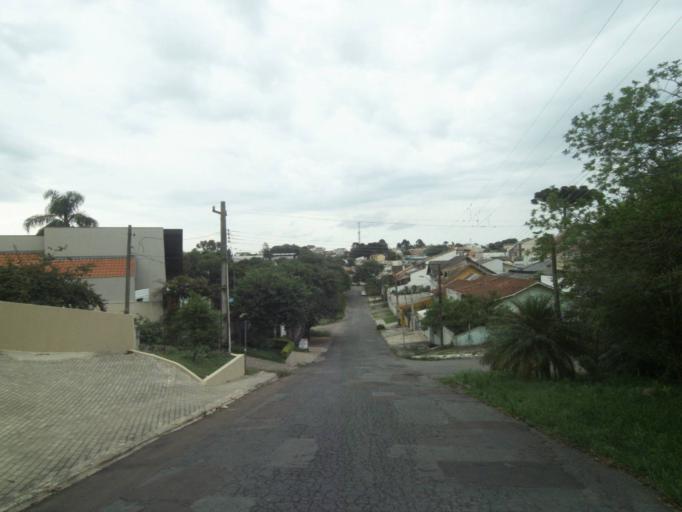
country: BR
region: Parana
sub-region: Curitiba
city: Curitiba
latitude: -25.3989
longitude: -49.2905
